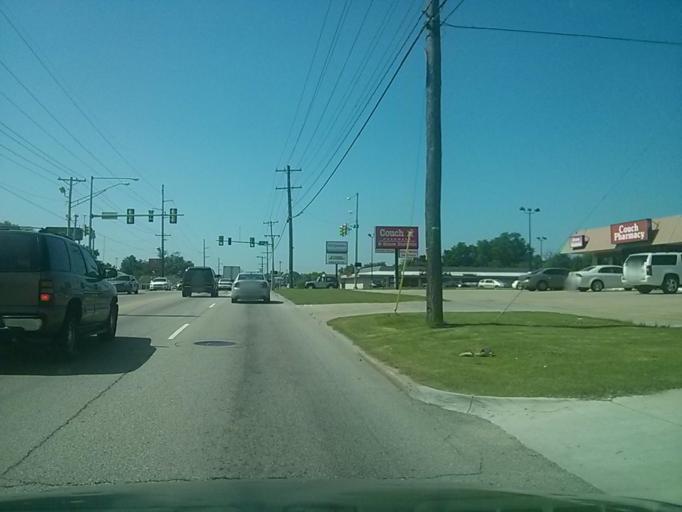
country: US
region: Oklahoma
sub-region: Tulsa County
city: Tulsa
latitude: 36.1558
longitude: -95.9046
